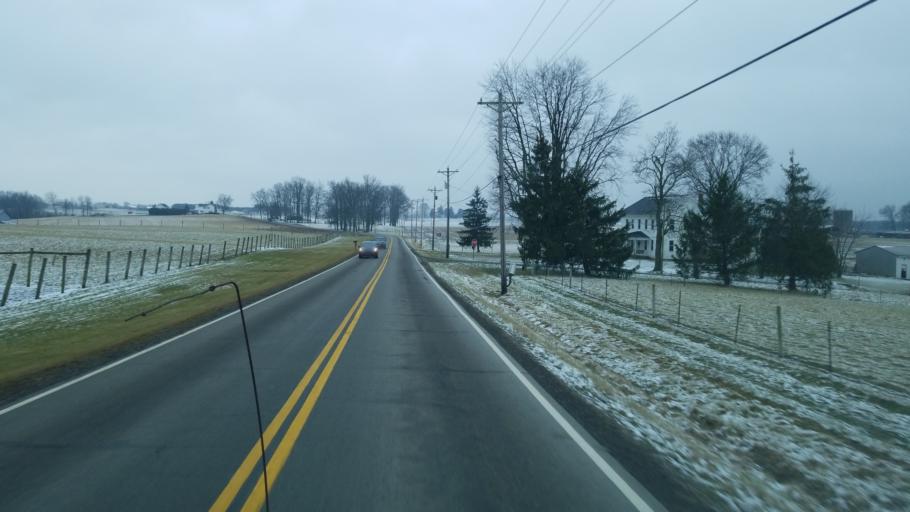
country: US
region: Ohio
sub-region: Wayne County
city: Apple Creek
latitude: 40.7313
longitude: -81.8962
